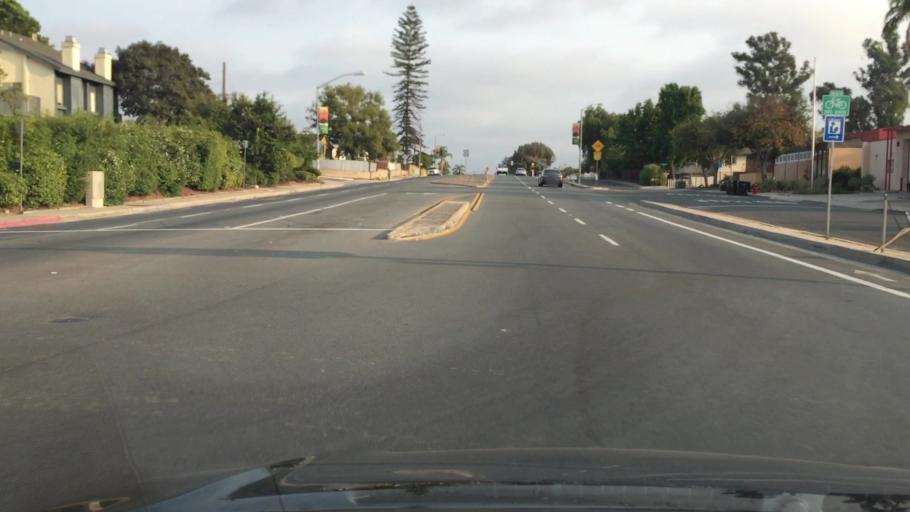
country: US
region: California
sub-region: San Diego County
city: Lemon Grove
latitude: 32.7358
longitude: -117.0797
